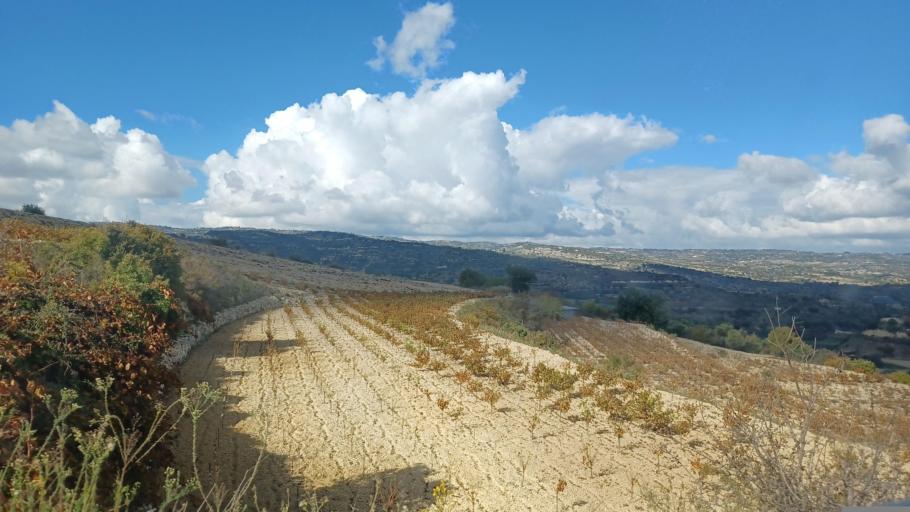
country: CY
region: Pafos
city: Mesogi
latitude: 34.8321
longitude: 32.5489
